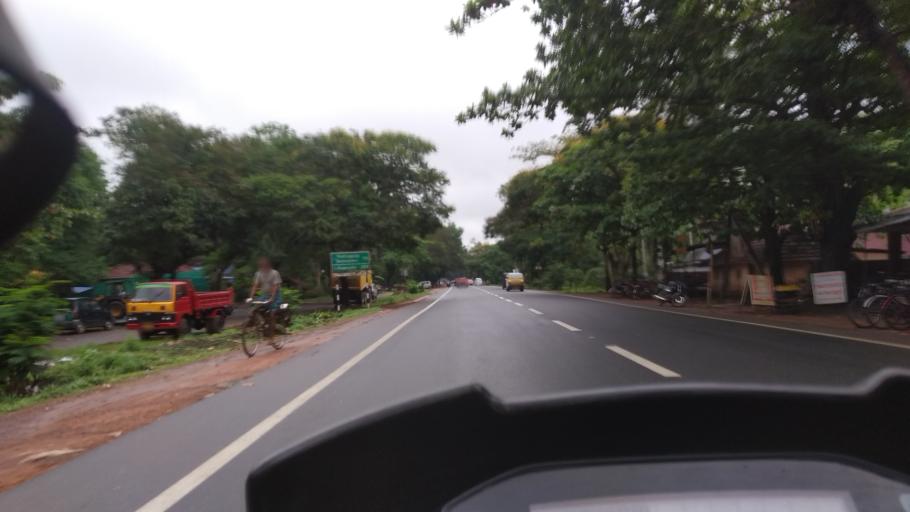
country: IN
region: Kerala
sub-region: Alappuzha
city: Mavelikara
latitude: 9.3034
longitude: 76.4326
